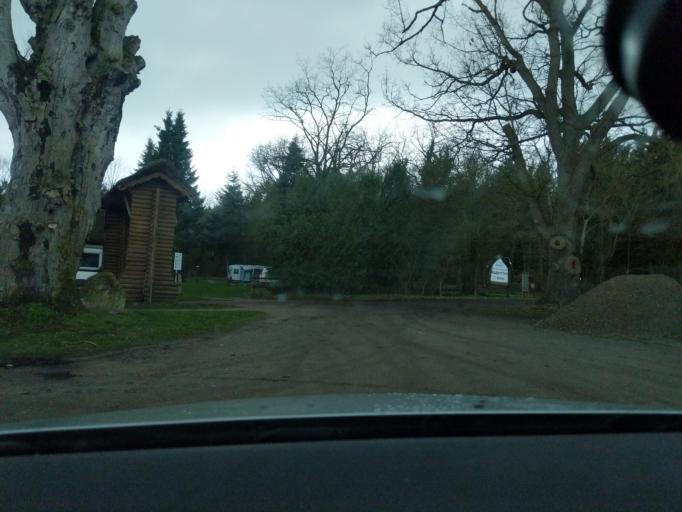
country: DE
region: Lower Saxony
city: Kranenburg
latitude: 53.6256
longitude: 9.2033
